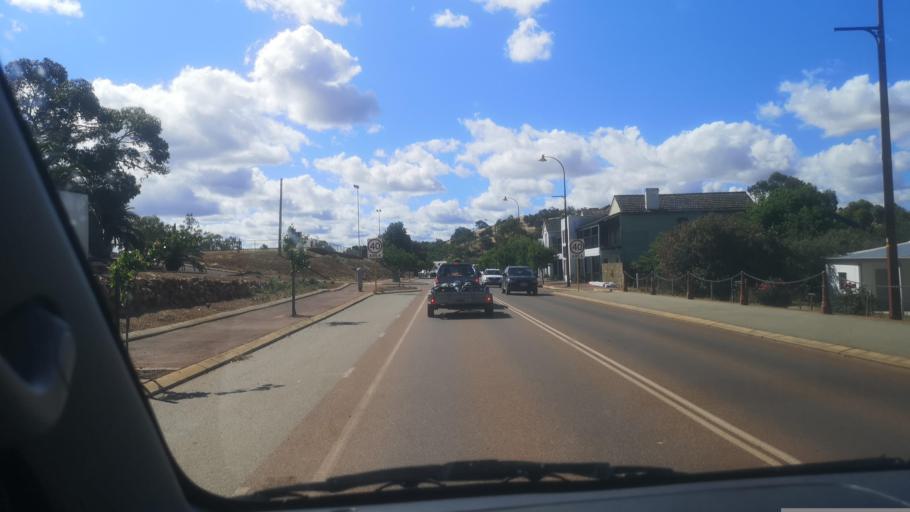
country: AU
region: Western Australia
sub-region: Toodyay
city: Toodyay
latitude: -31.5520
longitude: 116.4712
